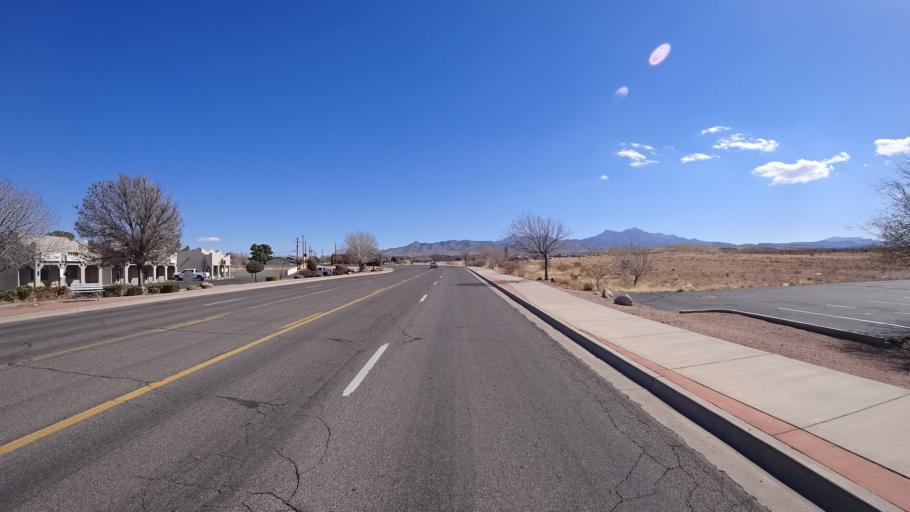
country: US
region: Arizona
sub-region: Mohave County
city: Kingman
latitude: 35.1917
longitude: -114.0239
